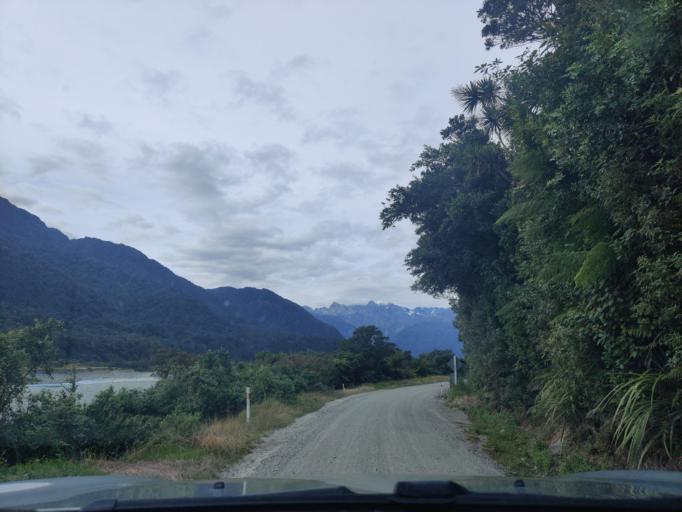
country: NZ
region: West Coast
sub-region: Westland District
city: Hokitika
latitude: -43.2877
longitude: 170.4042
